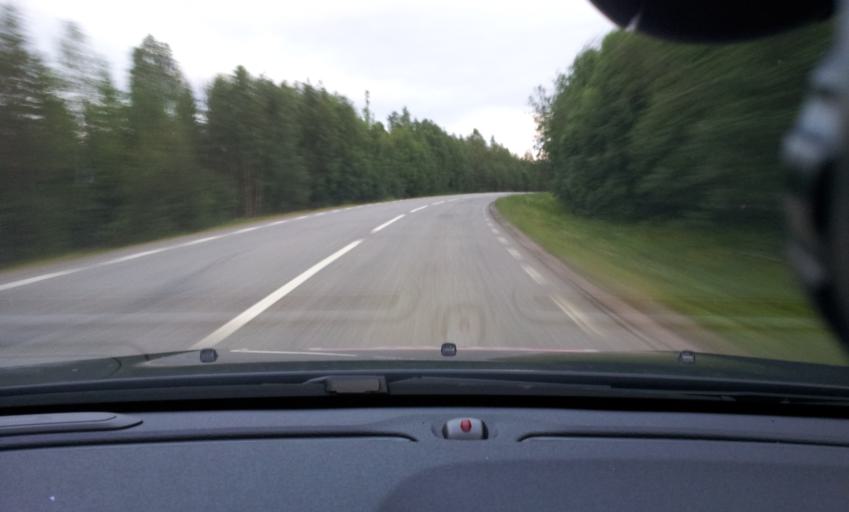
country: SE
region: Jaemtland
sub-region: Ragunda Kommun
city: Hammarstrand
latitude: 63.0415
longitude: 16.3906
